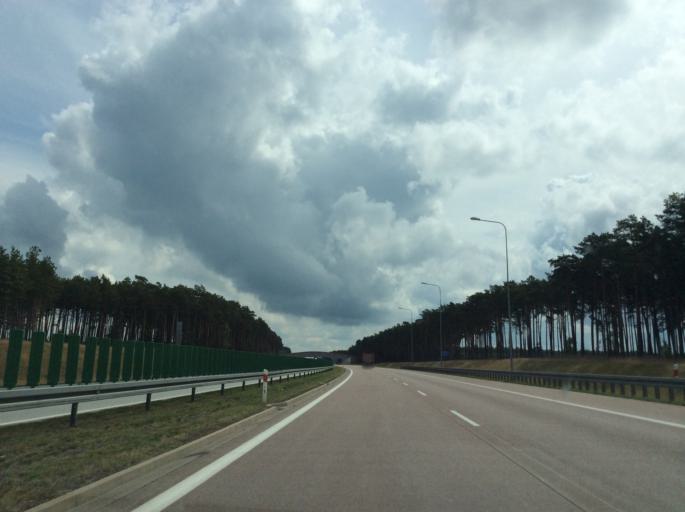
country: PL
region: Lubusz
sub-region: Powiat slubicki
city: Slubice
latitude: 52.3240
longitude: 14.6652
